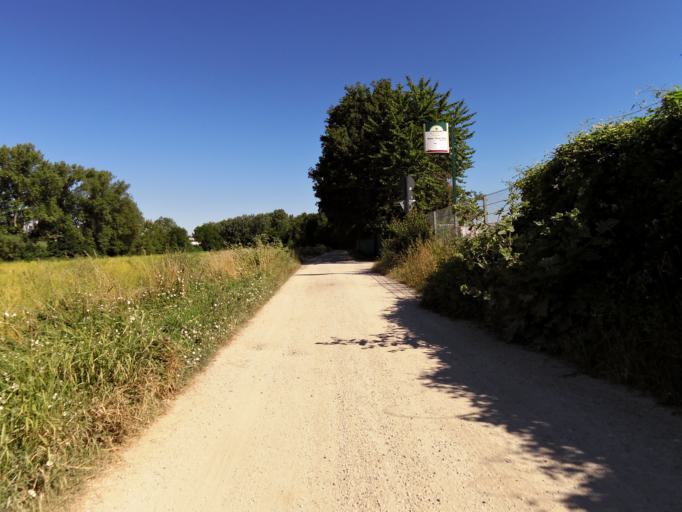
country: DE
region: Rheinland-Pfalz
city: Worms
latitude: 49.6197
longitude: 8.3839
